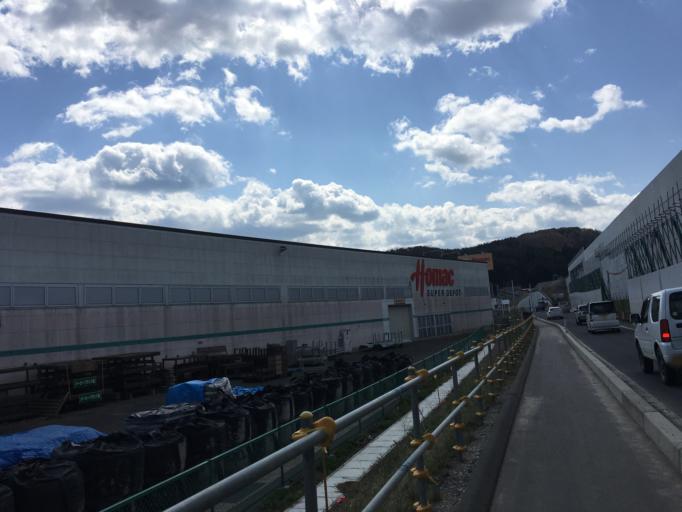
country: JP
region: Aomori
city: Hachinohe
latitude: 40.1903
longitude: 141.7873
